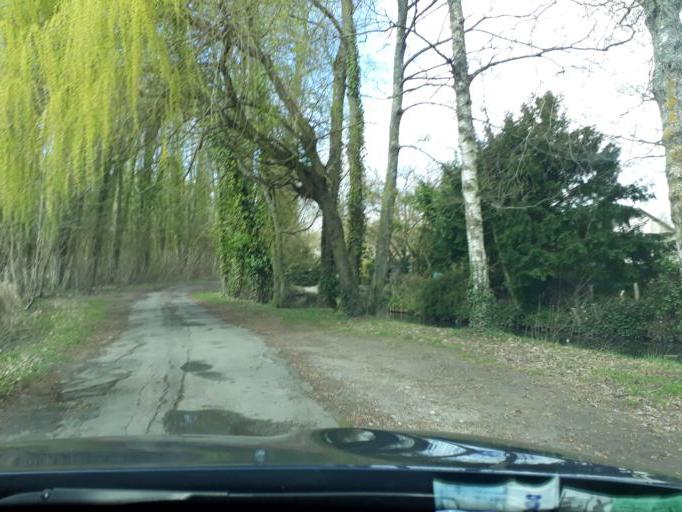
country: FR
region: Centre
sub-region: Departement du Loiret
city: Meung-sur-Loire
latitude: 47.8358
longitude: 1.7019
